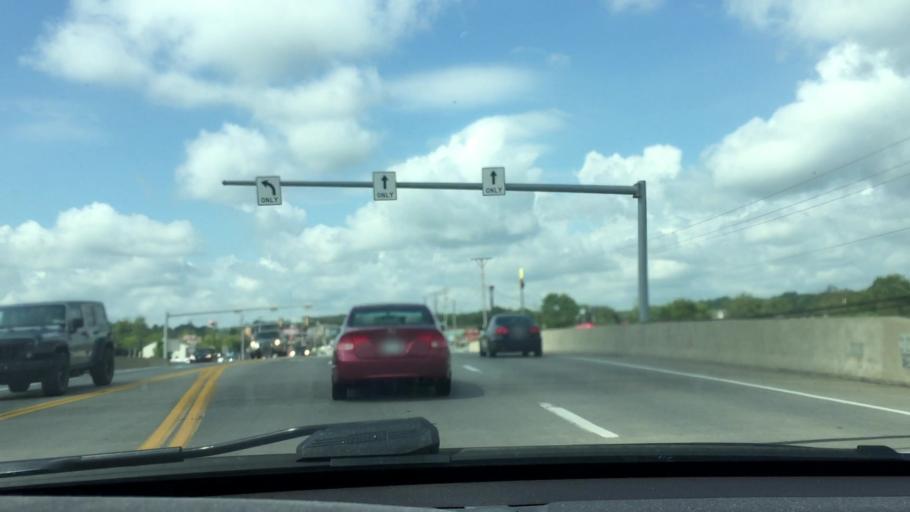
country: US
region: Pennsylvania
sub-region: Mercer County
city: Grove City
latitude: 41.1435
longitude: -80.1545
